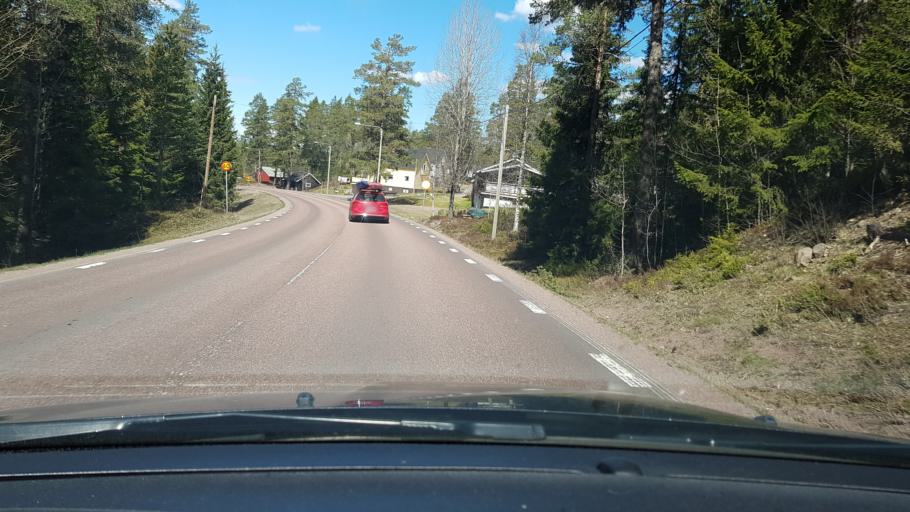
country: SE
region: Dalarna
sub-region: Malung-Saelens kommun
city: Malung
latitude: 61.0653
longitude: 13.3370
